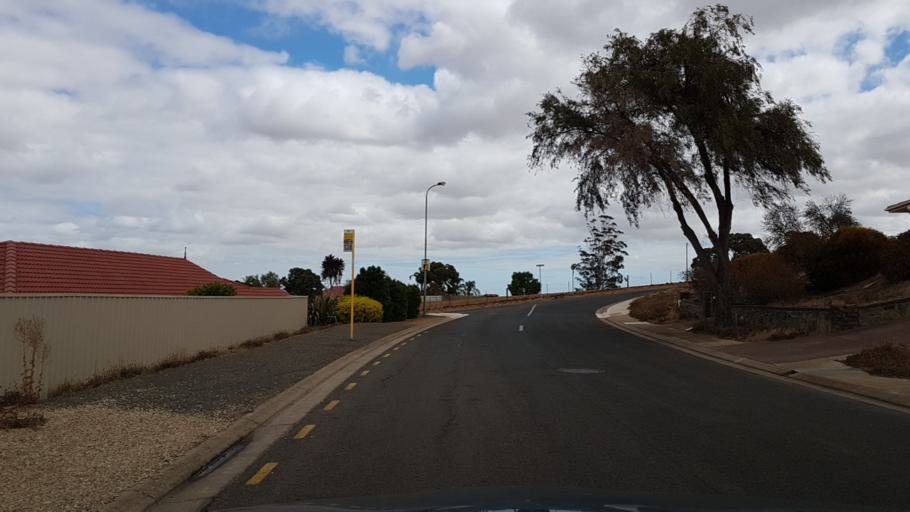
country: AU
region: South Australia
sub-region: Gawler
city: Gawler
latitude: -34.6060
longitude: 138.7579
